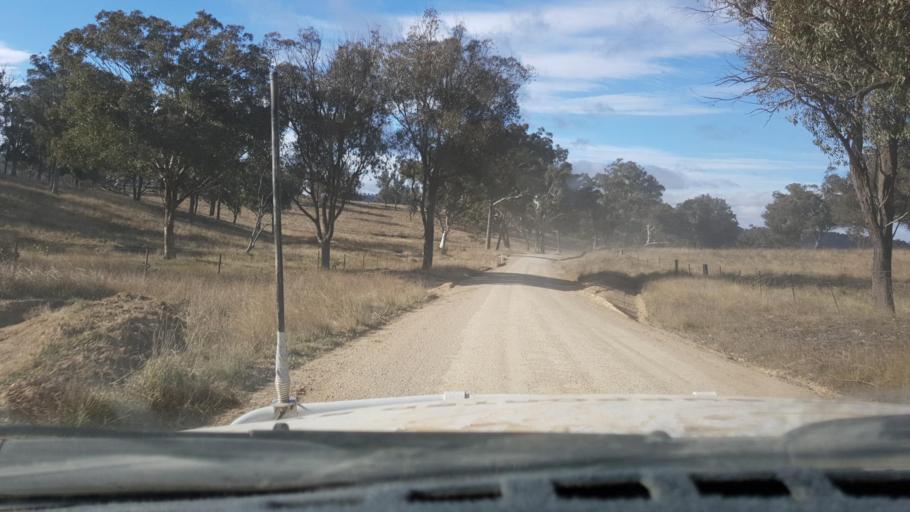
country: AU
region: New South Wales
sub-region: Armidale Dumaresq
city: Enmore
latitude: -30.7580
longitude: 151.6300
